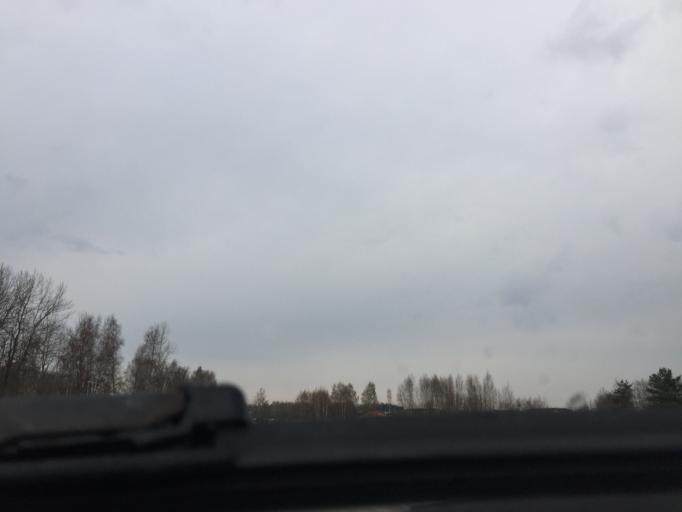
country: EE
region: Tartu
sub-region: UElenurme vald
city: Ulenurme
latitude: 58.3027
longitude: 26.7245
